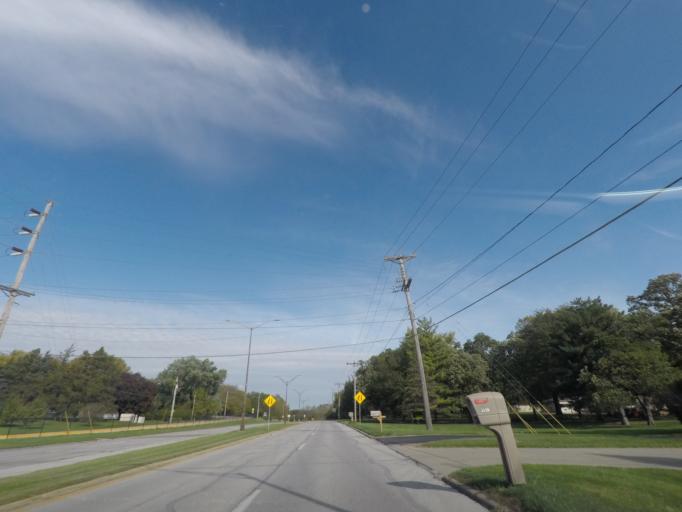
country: US
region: Iowa
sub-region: Story County
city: Ames
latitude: 42.0565
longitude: -93.6206
